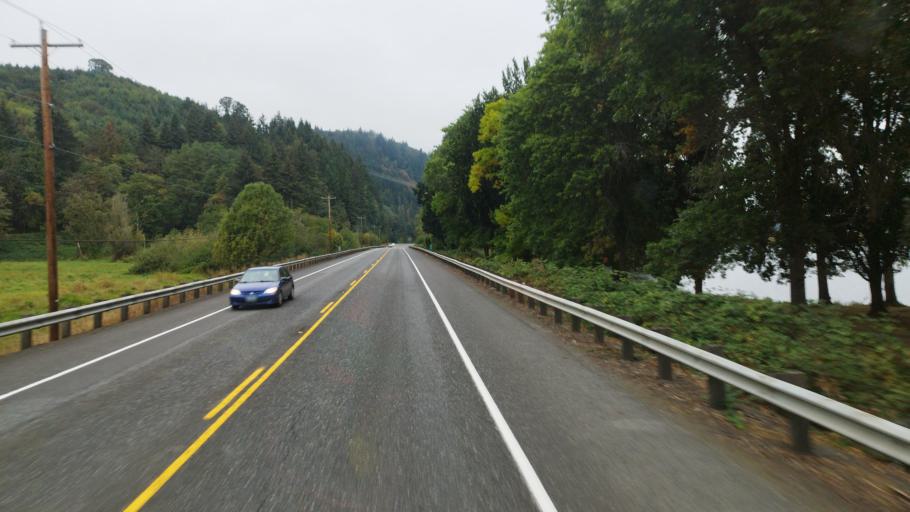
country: US
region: Washington
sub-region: Cowlitz County
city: Kalama
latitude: 46.0323
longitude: -122.8902
